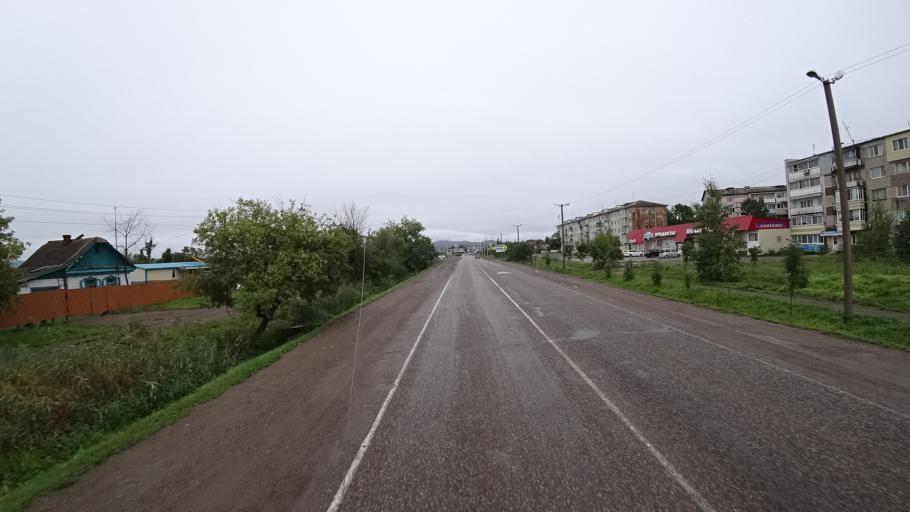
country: RU
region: Primorskiy
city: Monastyrishche
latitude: 44.2061
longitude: 132.4501
